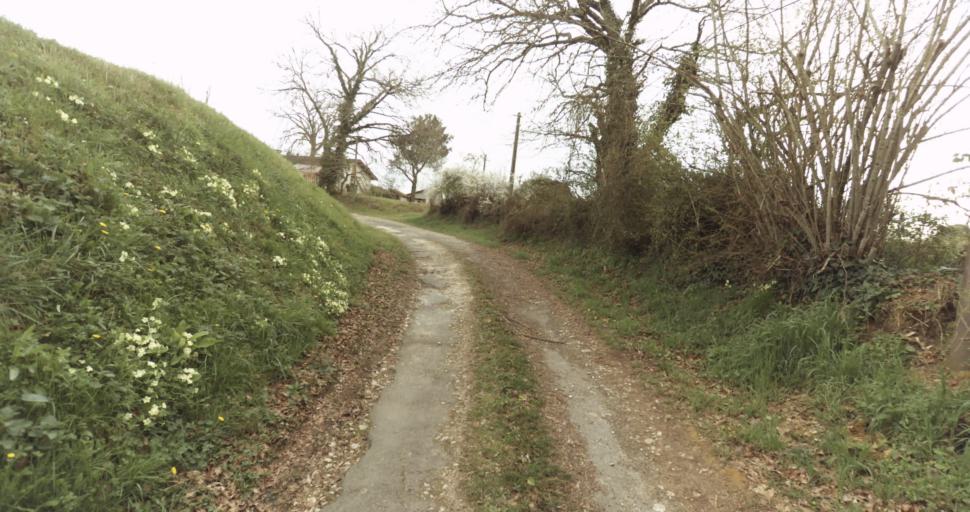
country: FR
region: Aquitaine
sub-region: Departement des Landes
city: Roquefort
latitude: 44.0318
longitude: -0.3315
